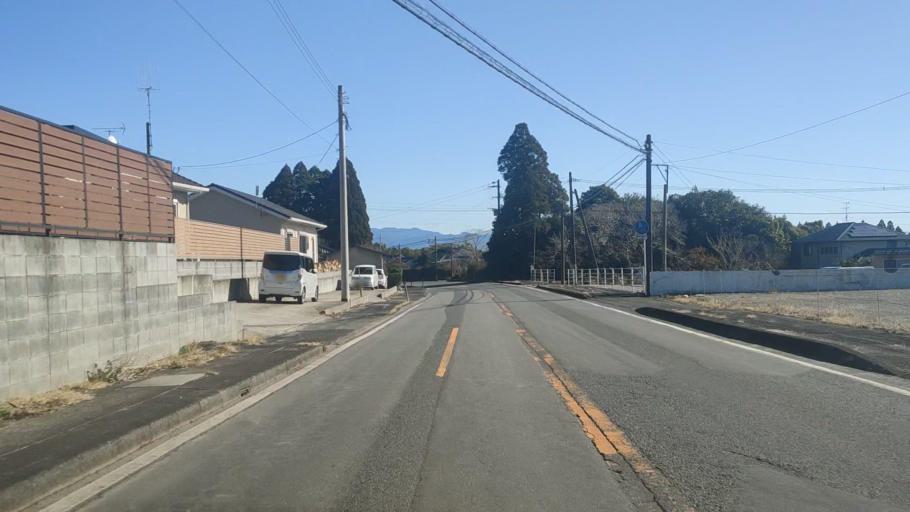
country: JP
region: Kagoshima
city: Sueyoshicho-ninokata
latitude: 31.6954
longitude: 130.9932
